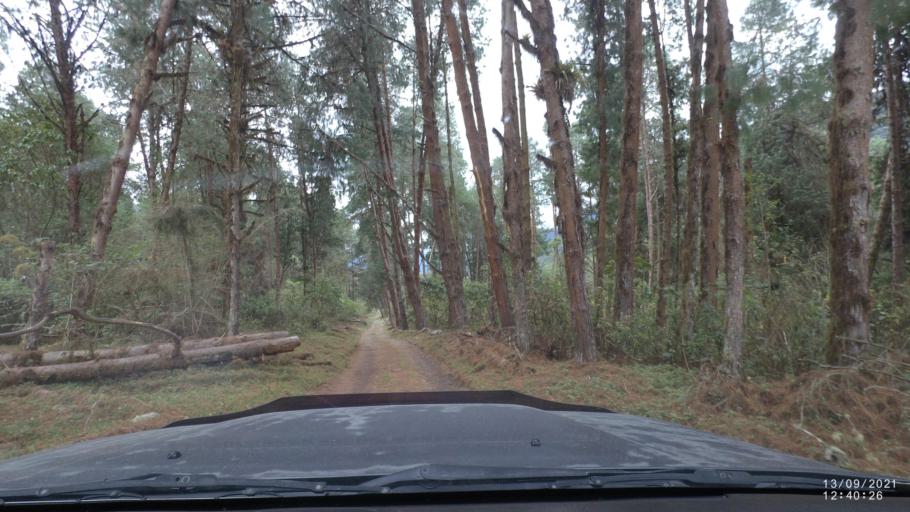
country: BO
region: Cochabamba
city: Colomi
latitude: -17.2586
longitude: -65.8156
